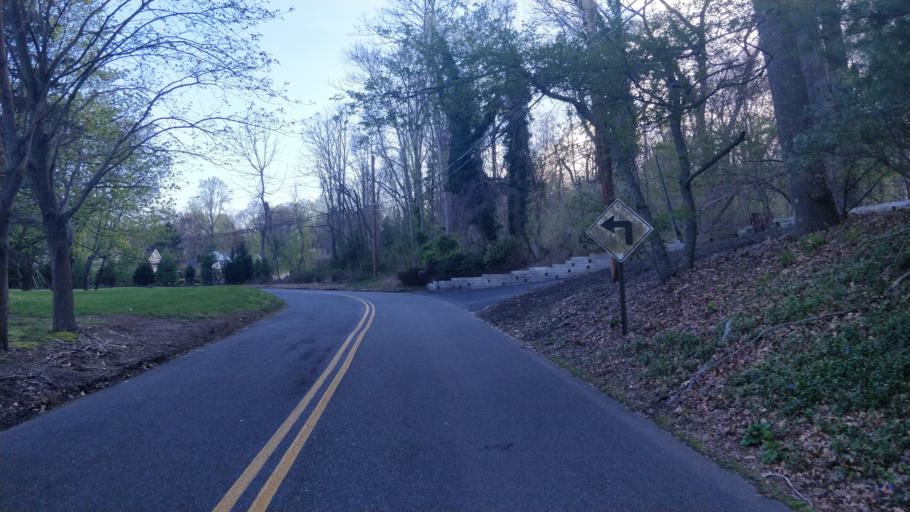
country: US
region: New York
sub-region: Suffolk County
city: Nissequogue
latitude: 40.8920
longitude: -73.1889
